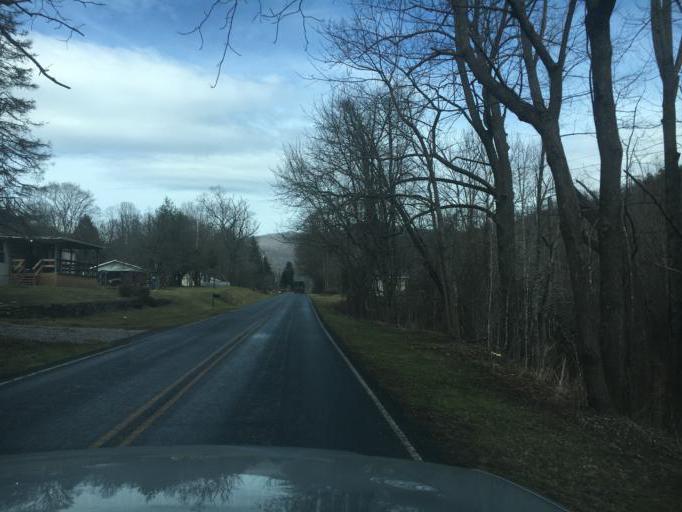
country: US
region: North Carolina
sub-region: Haywood County
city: Canton
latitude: 35.4237
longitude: -82.8137
